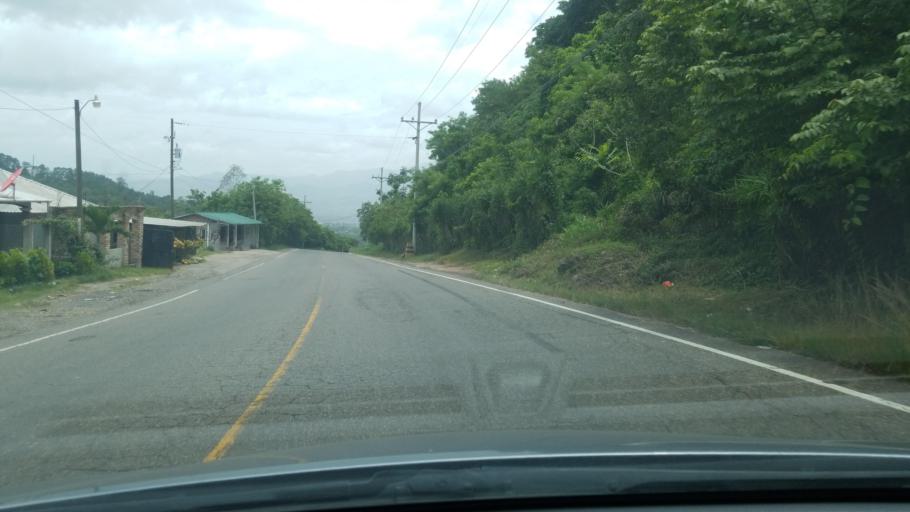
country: HN
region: Copan
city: Ojos de Agua
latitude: 14.6750
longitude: -88.8217
